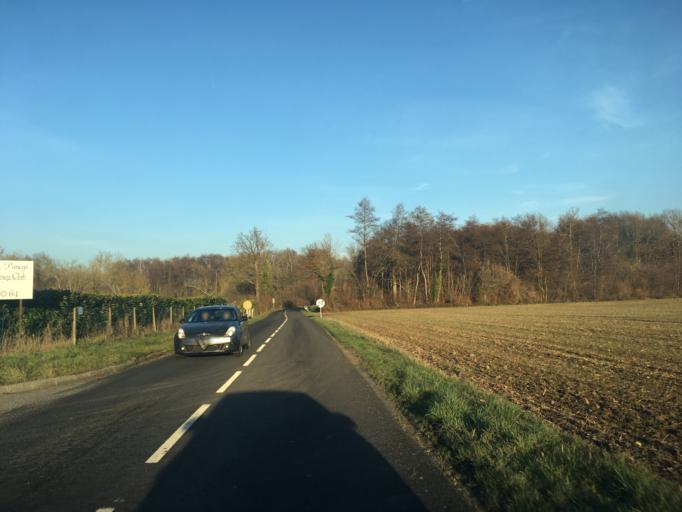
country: FR
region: Haute-Normandie
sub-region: Departement de l'Eure
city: Menilles
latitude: 49.0464
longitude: 1.3105
